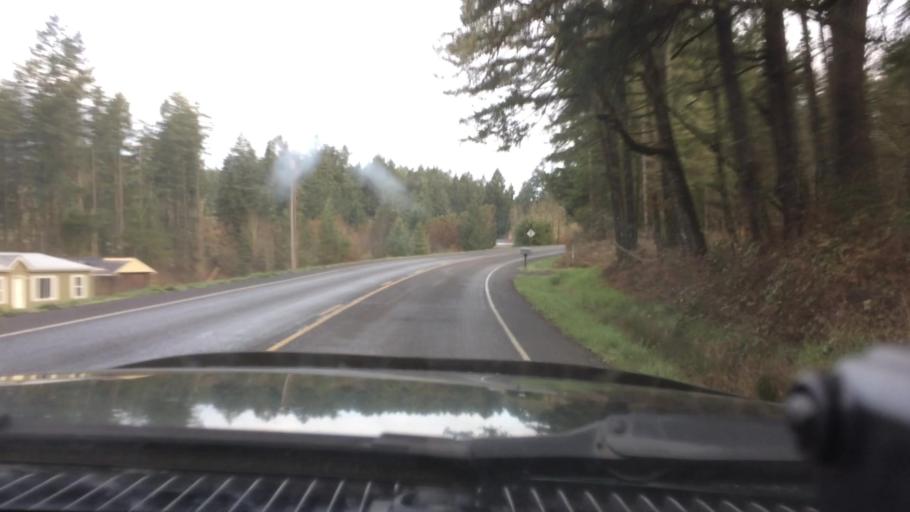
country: US
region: Oregon
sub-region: Lane County
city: Veneta
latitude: 44.1235
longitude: -123.3488
